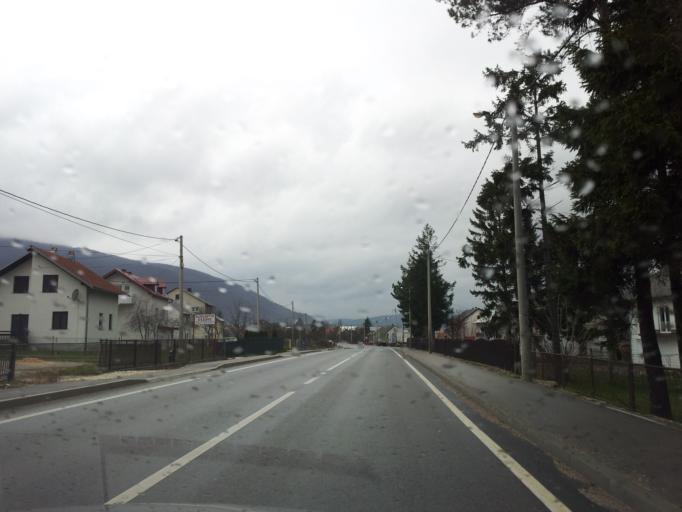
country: BA
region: Federation of Bosnia and Herzegovina
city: Izacic
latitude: 44.7375
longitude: 15.7176
